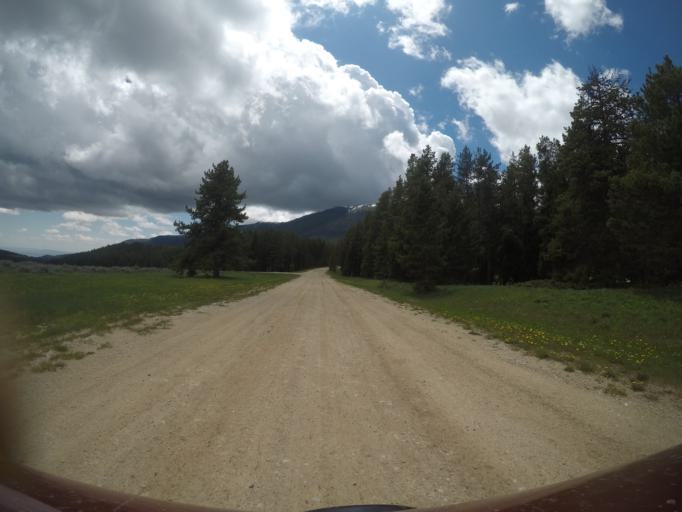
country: US
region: Wyoming
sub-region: Big Horn County
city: Lovell
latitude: 45.1783
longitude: -108.4490
